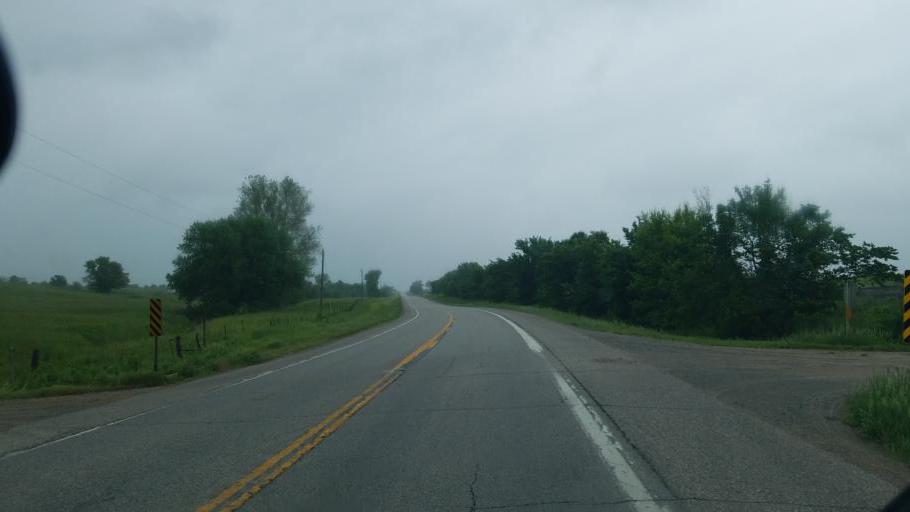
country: US
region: Missouri
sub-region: Carroll County
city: Carrollton
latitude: 39.4705
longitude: -93.4761
